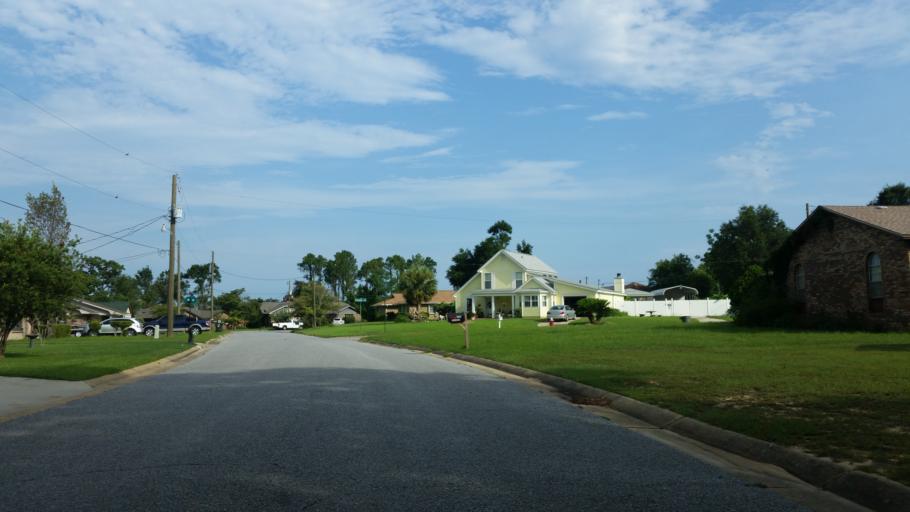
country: US
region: Florida
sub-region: Escambia County
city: Ferry Pass
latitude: 30.5127
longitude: -87.1770
